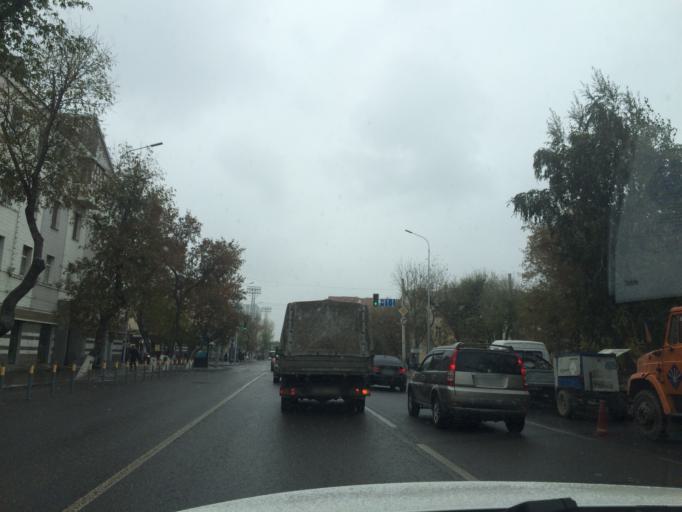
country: KZ
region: Astana Qalasy
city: Astana
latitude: 51.1643
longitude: 71.4182
